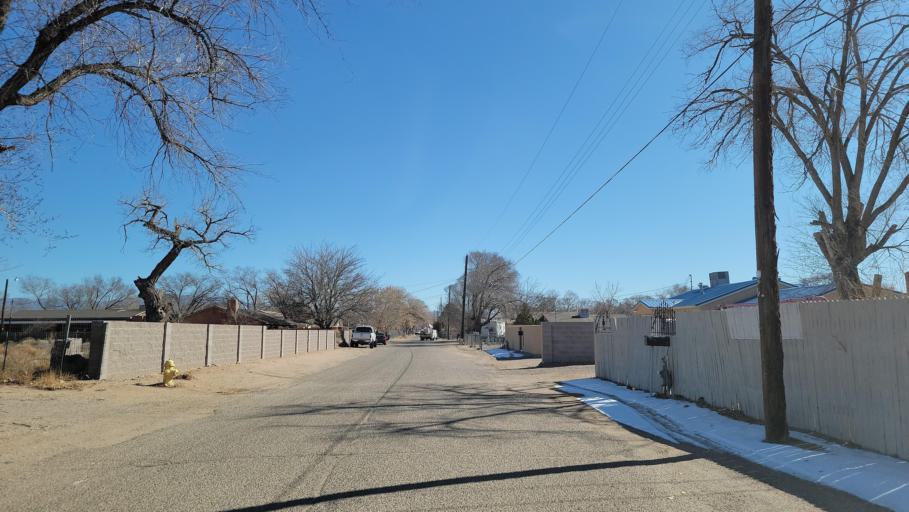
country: US
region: New Mexico
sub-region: Bernalillo County
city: South Valley
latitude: 35.0322
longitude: -106.6830
